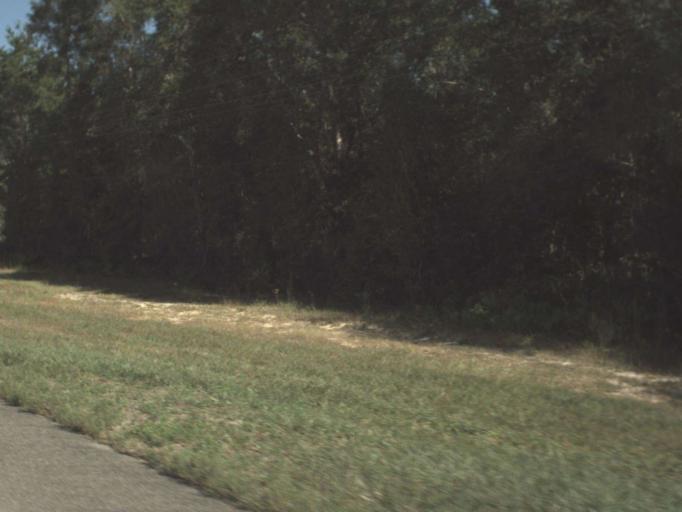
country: US
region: Florida
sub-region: Walton County
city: Freeport
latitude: 30.5603
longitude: -85.9189
